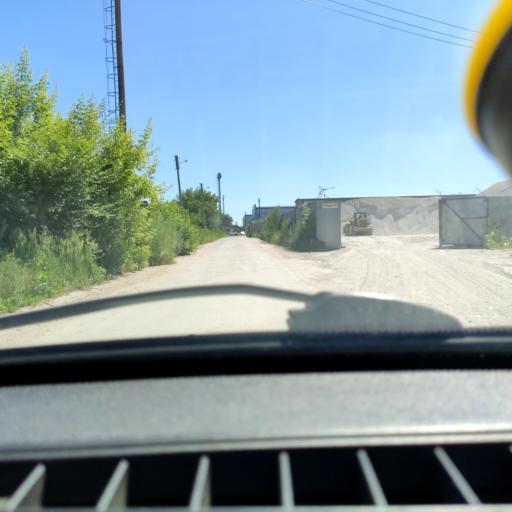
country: RU
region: Samara
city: Tol'yatti
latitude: 53.5743
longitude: 49.2994
